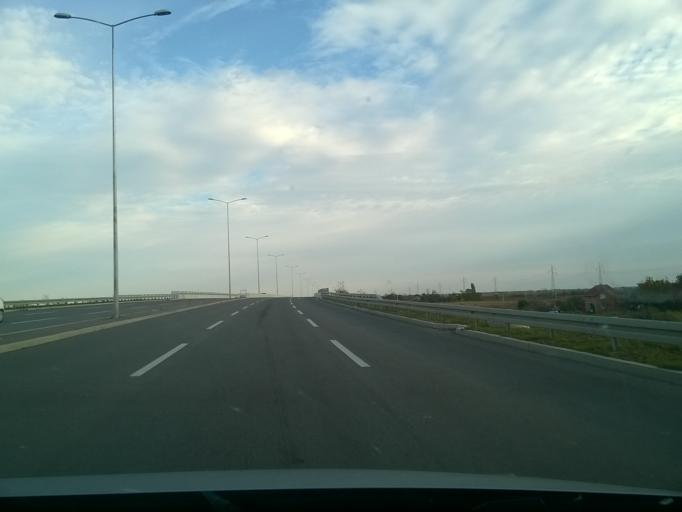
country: RS
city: Ovca
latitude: 44.8618
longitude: 20.5142
